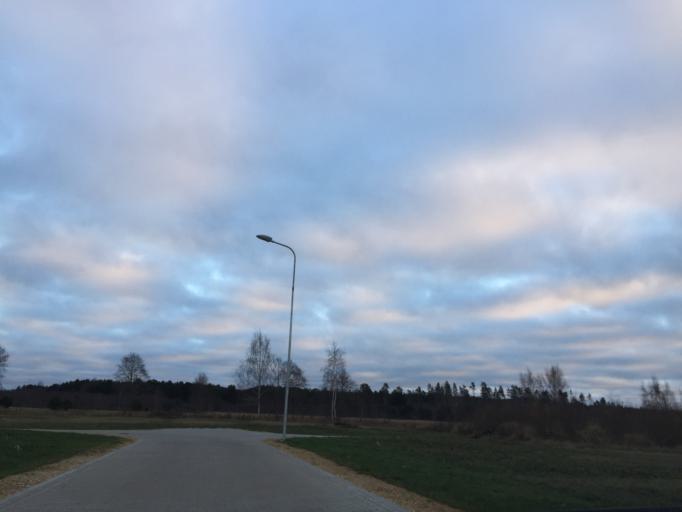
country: LV
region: Adazi
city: Adazi
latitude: 57.0662
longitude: 24.3447
